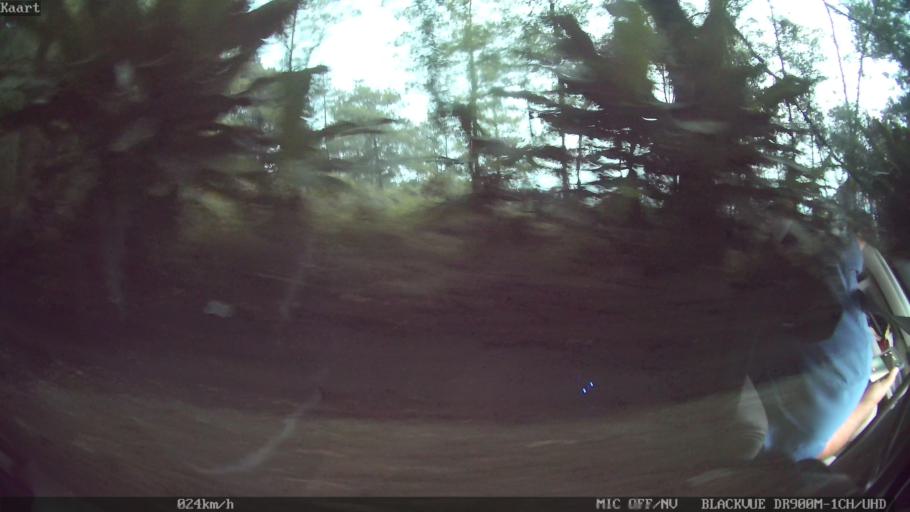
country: ID
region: Bali
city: Banjar Kedisan
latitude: -8.2640
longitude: 115.3330
